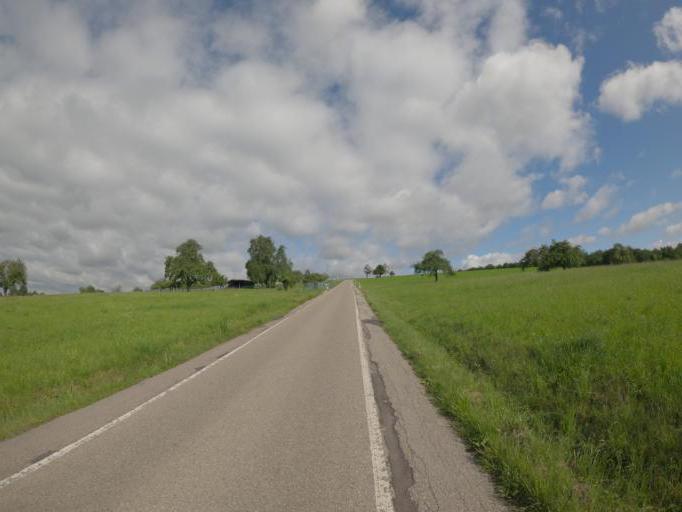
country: DE
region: Baden-Wuerttemberg
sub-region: Regierungsbezirk Stuttgart
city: Ebersbach an der Fils
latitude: 48.7306
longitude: 9.5383
